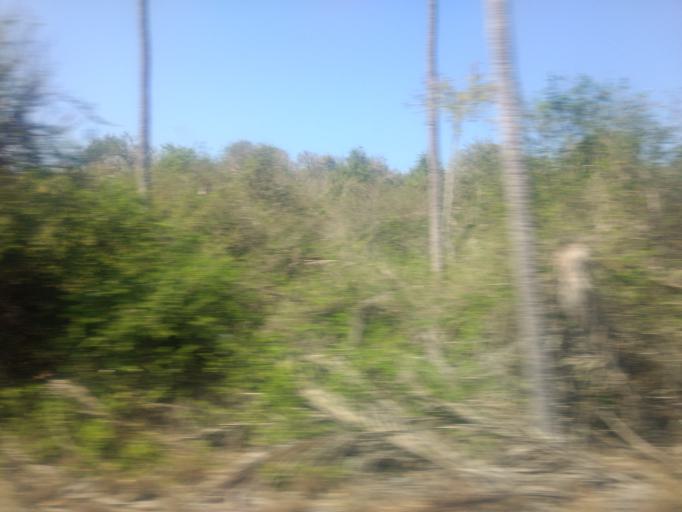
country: MX
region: Colima
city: El Colomo
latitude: 18.9794
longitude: -104.1939
